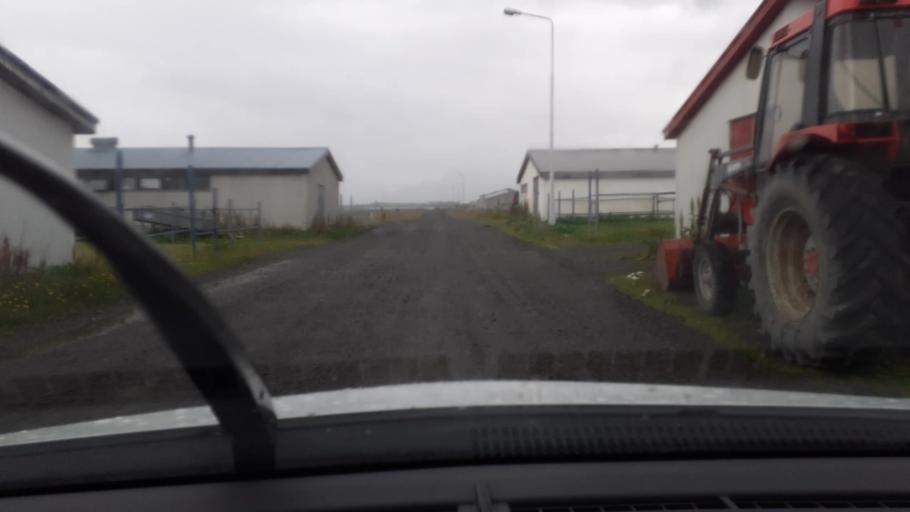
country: IS
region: West
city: Akranes
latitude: 64.3411
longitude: -22.0233
